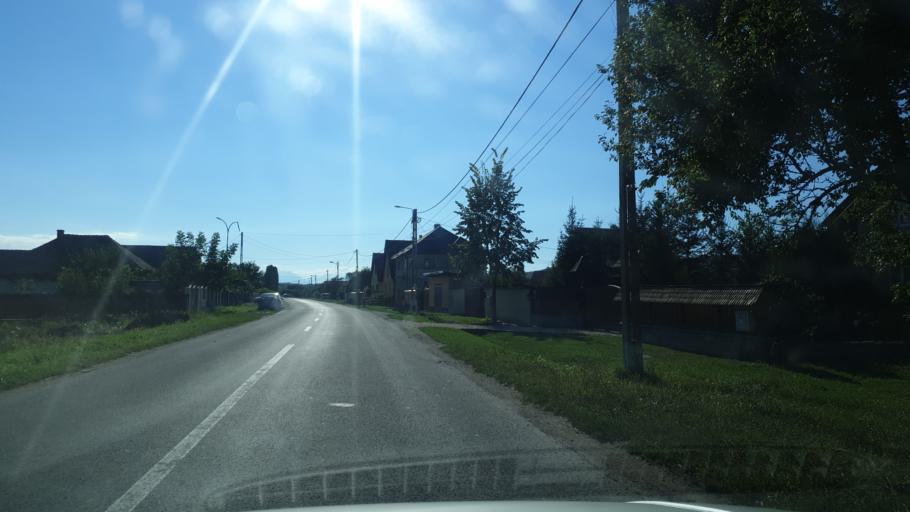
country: RO
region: Covasna
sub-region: Comuna Ilieni
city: Ilieni
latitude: 45.7643
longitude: 25.7270
